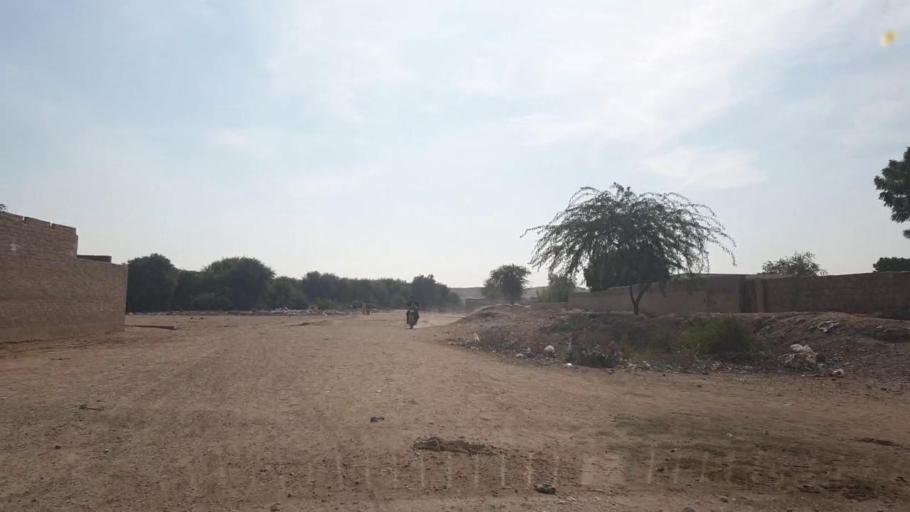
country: PK
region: Sindh
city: Hala
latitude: 25.7413
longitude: 68.2943
